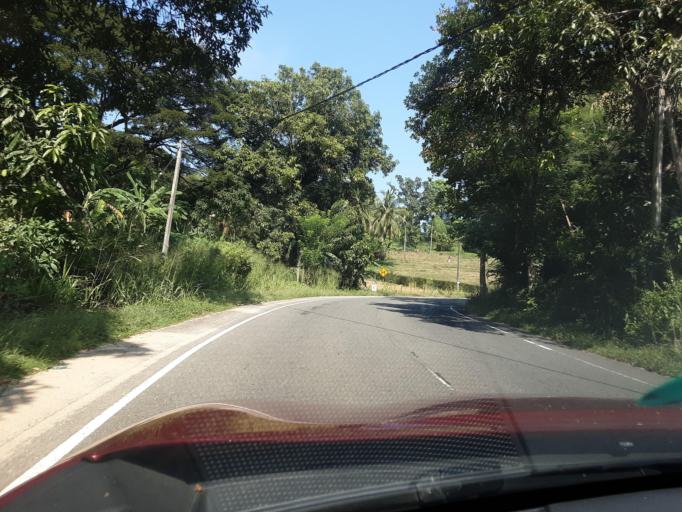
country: LK
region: Uva
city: Badulla
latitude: 7.1546
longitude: 81.0553
